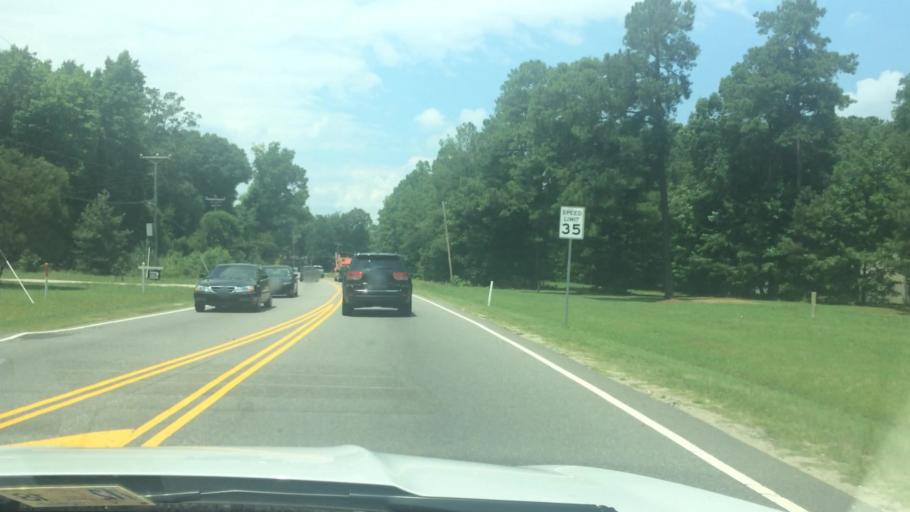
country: US
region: Virginia
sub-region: York County
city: Yorktown
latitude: 37.1817
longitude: -76.5705
